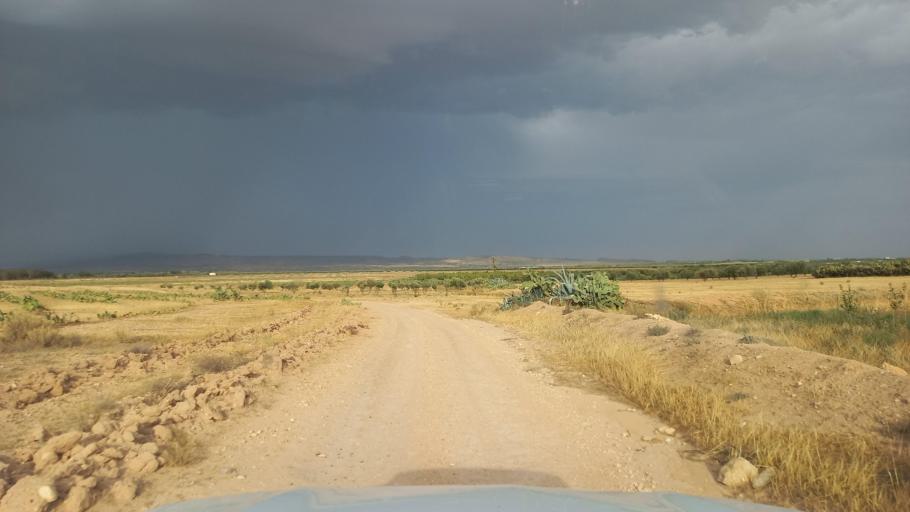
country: TN
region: Al Qasrayn
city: Kasserine
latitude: 35.2874
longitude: 9.0434
